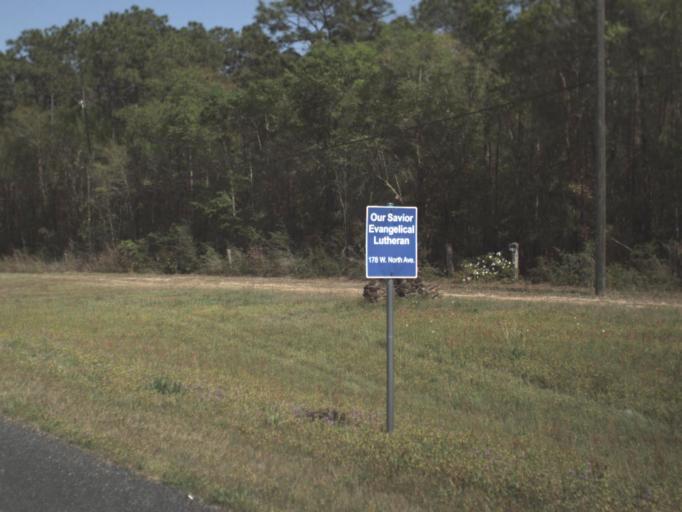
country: US
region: Florida
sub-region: Okaloosa County
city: Crestview
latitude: 30.7632
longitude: -86.6032
